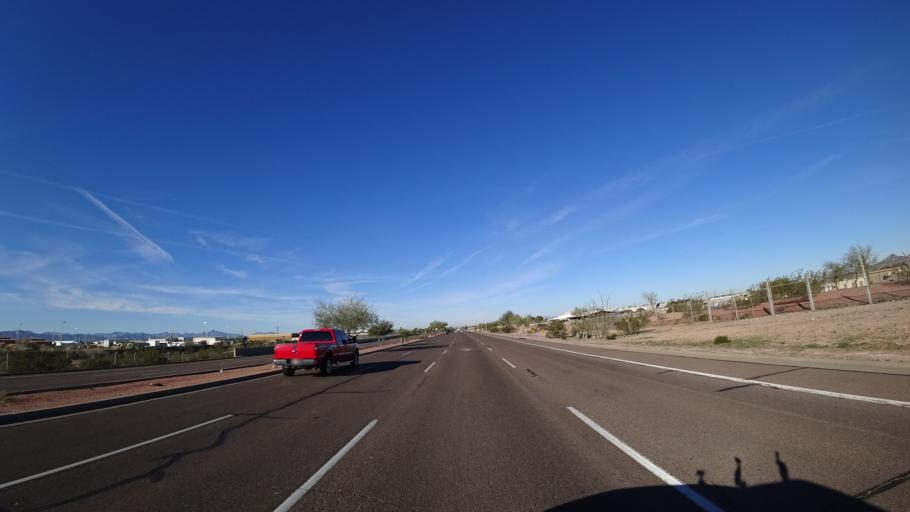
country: US
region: Arizona
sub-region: Maricopa County
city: Tempe Junction
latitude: 33.4656
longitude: -111.9651
